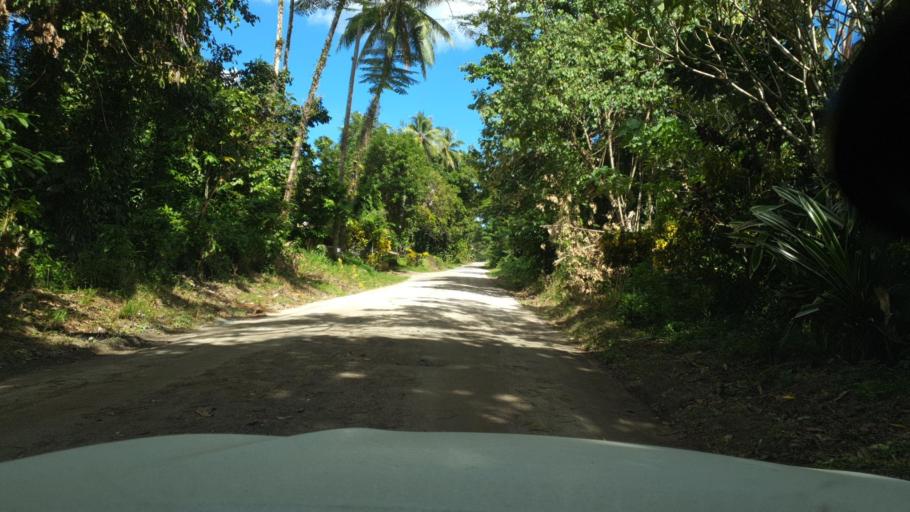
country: SB
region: Guadalcanal
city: Honiara
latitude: -9.2807
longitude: 159.6422
